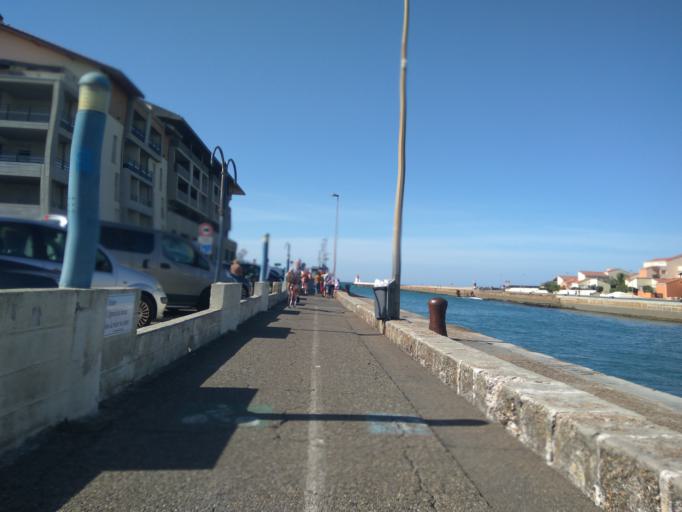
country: FR
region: Aquitaine
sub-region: Departement des Landes
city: Capbreton
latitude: 43.6545
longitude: -1.4429
